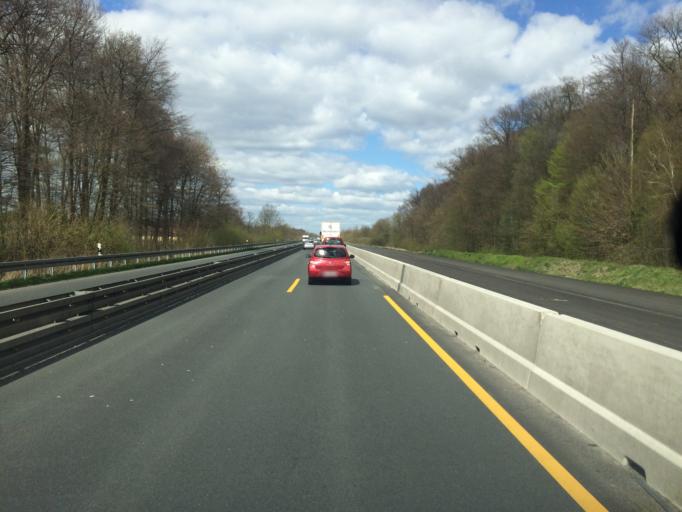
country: DE
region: North Rhine-Westphalia
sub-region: Regierungsbezirk Munster
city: Legden
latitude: 52.0353
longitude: 7.0616
